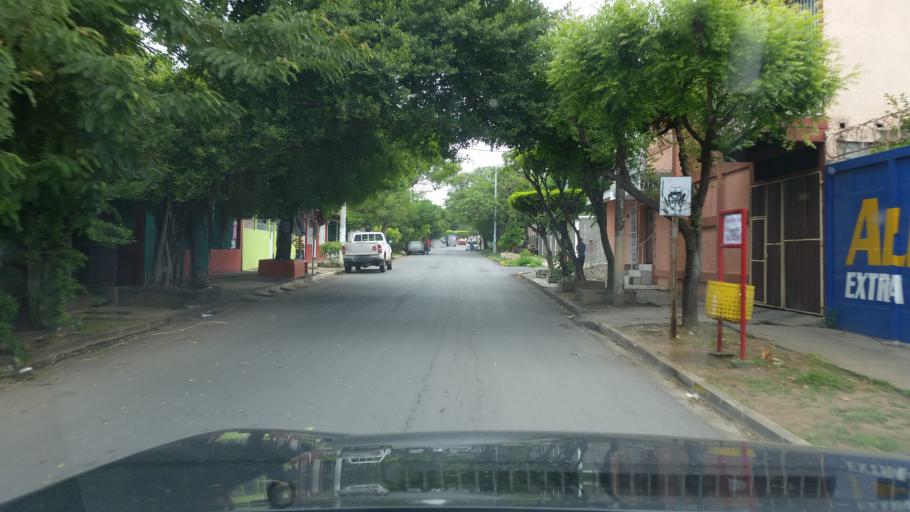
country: NI
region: Managua
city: Managua
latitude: 12.1237
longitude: -86.2189
